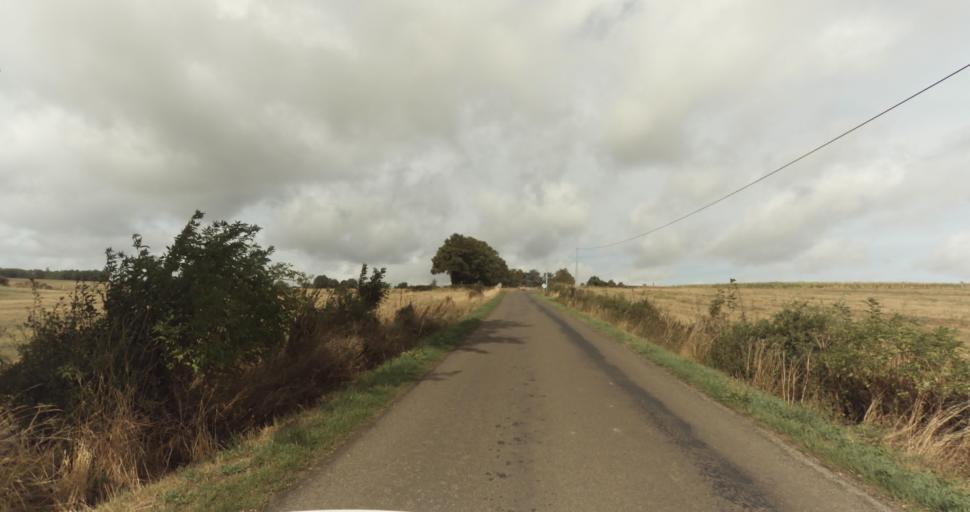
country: FR
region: Lower Normandy
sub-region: Departement de l'Orne
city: Gace
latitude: 48.8386
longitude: 0.3788
